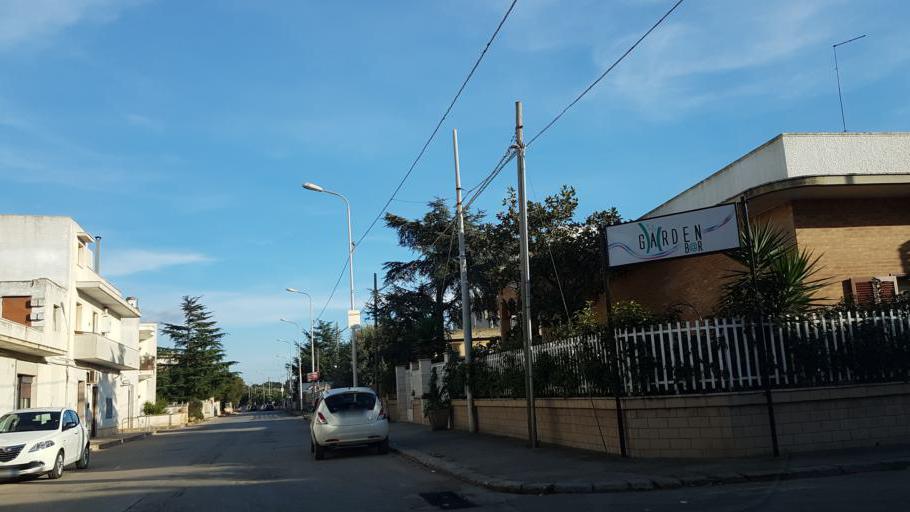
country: IT
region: Apulia
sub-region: Provincia di Brindisi
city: Carovigno
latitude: 40.7031
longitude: 17.6658
